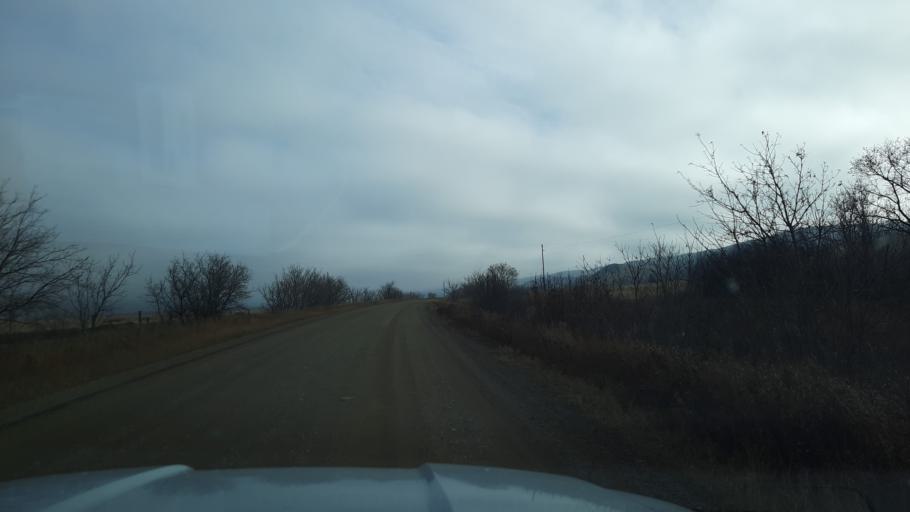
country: CA
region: Saskatchewan
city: Pilot Butte
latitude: 50.7850
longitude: -104.1790
